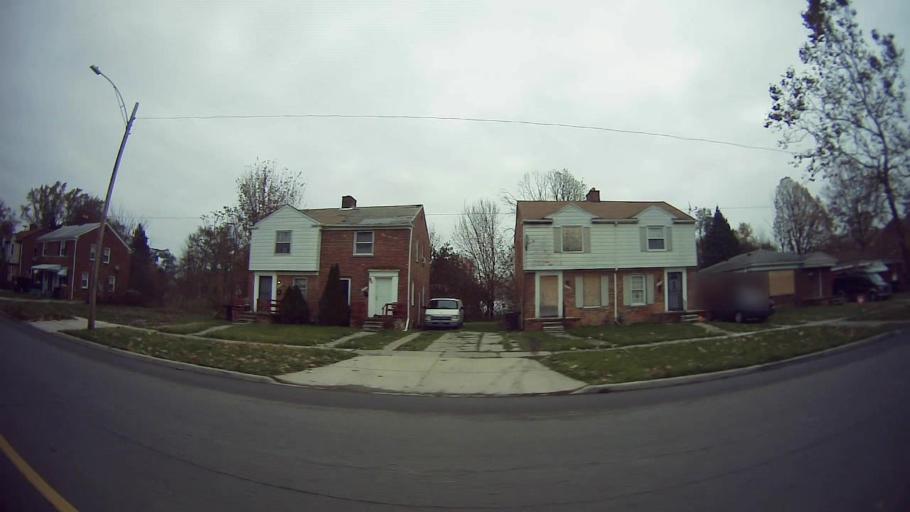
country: US
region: Michigan
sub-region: Wayne County
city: Dearborn Heights
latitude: 42.3492
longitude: -83.2356
